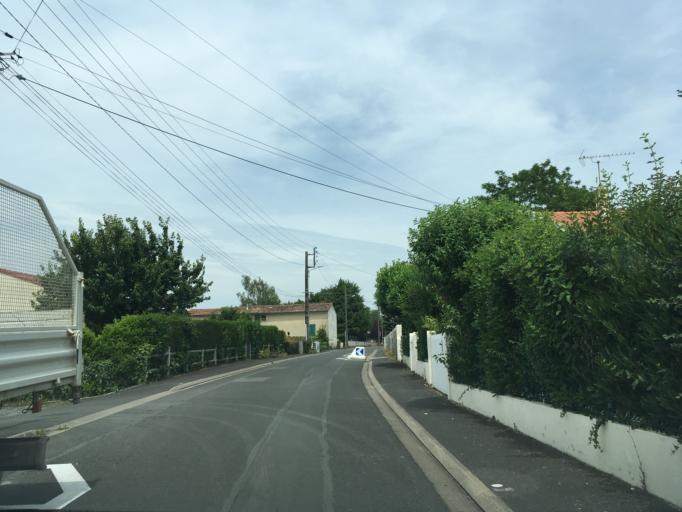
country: FR
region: Poitou-Charentes
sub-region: Departement des Deux-Sevres
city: Niort
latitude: 46.3221
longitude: -0.4855
